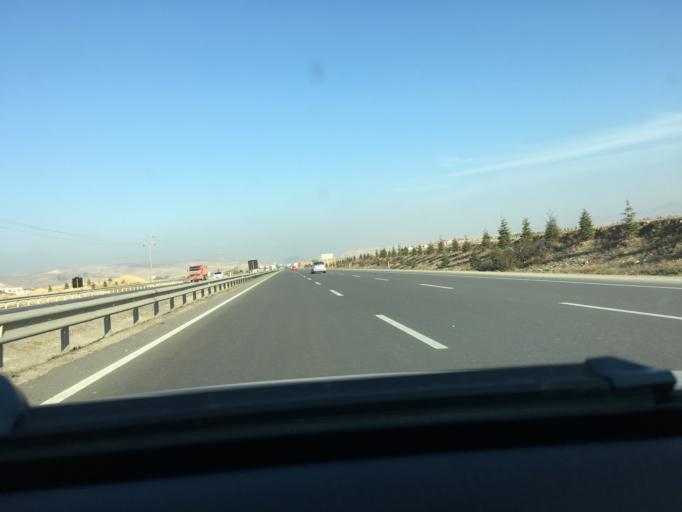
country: TR
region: Ankara
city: Temelli
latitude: 39.7456
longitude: 32.4179
